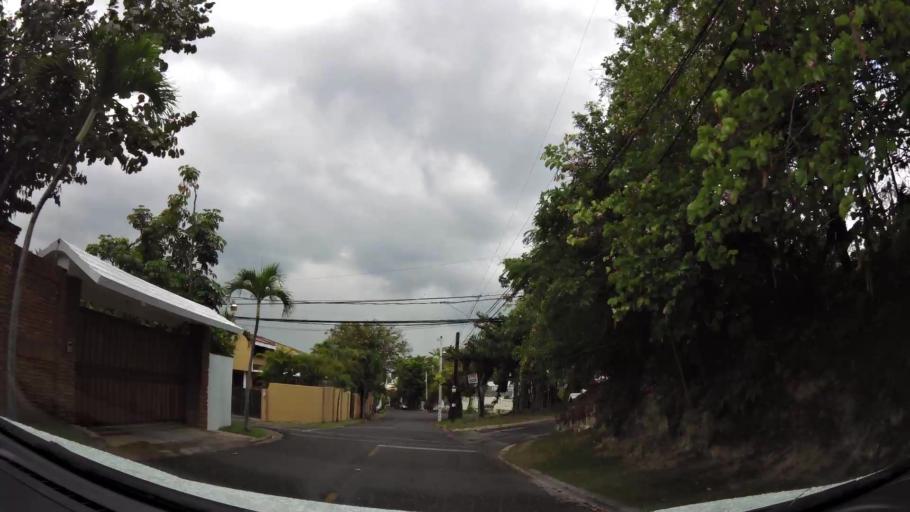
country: DO
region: Nacional
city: La Agustina
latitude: 18.4997
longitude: -69.9373
